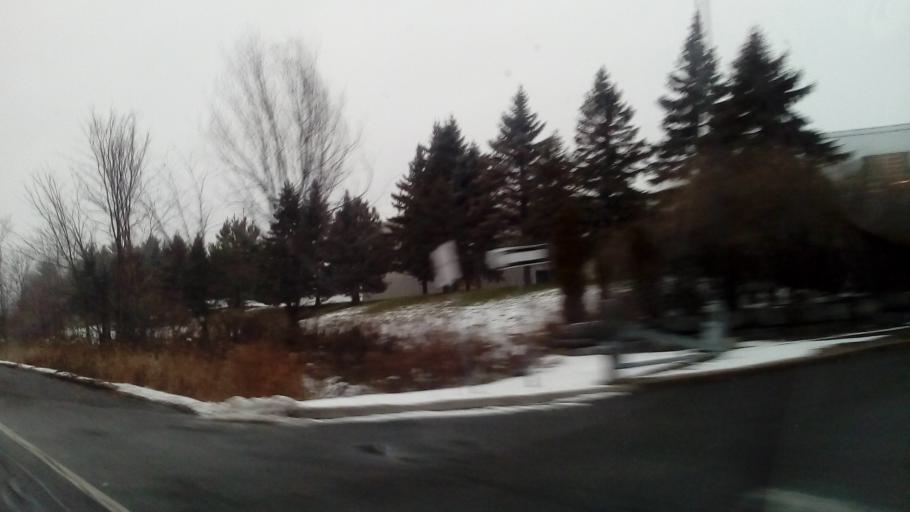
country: CA
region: Ontario
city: Ottawa
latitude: 45.4406
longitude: -75.5720
